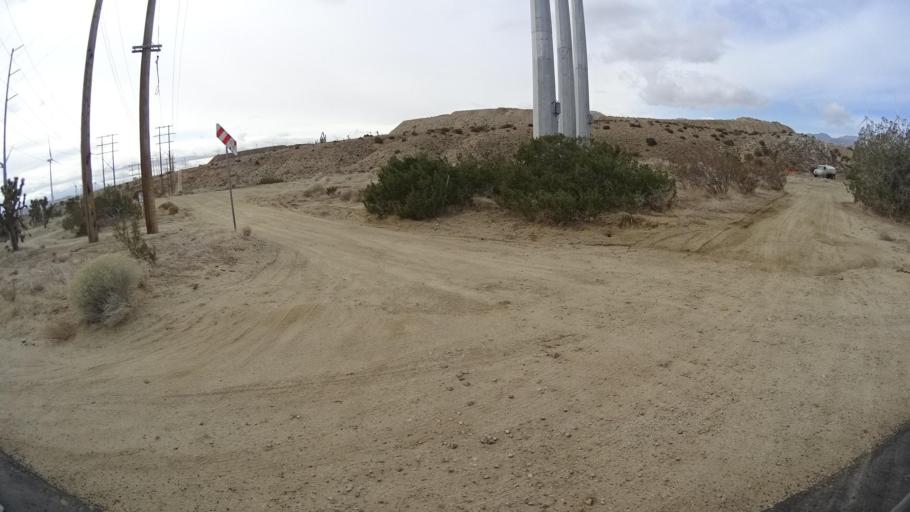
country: US
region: California
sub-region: Kern County
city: Mojave
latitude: 35.0435
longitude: -118.3102
